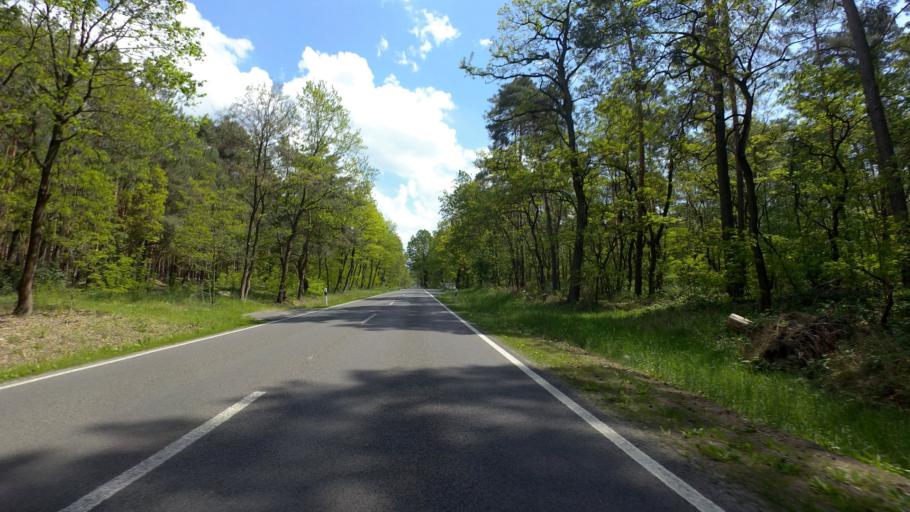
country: DE
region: Brandenburg
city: Luebben
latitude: 51.9433
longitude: 13.9399
